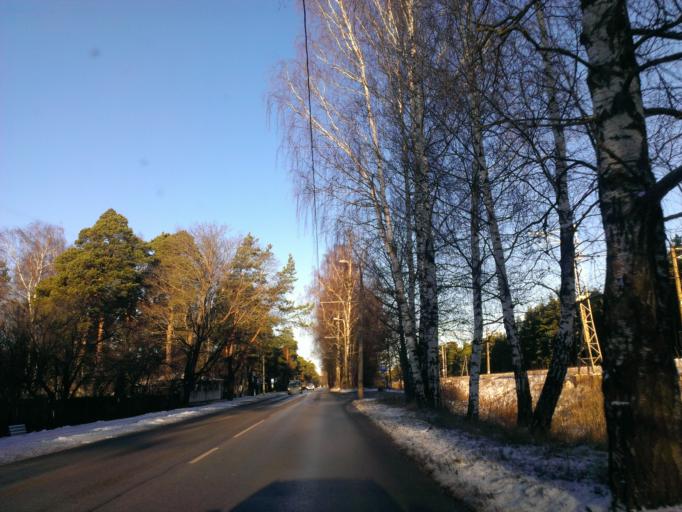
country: LV
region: Riga
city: Bolderaja
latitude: 57.0631
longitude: 24.1062
